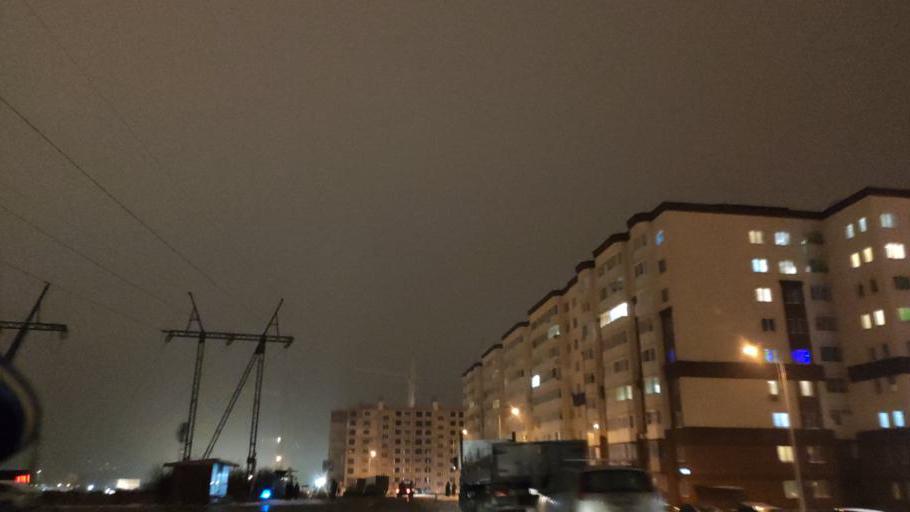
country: RU
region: Moscow
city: Zagor'ye
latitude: 55.5361
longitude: 37.6379
